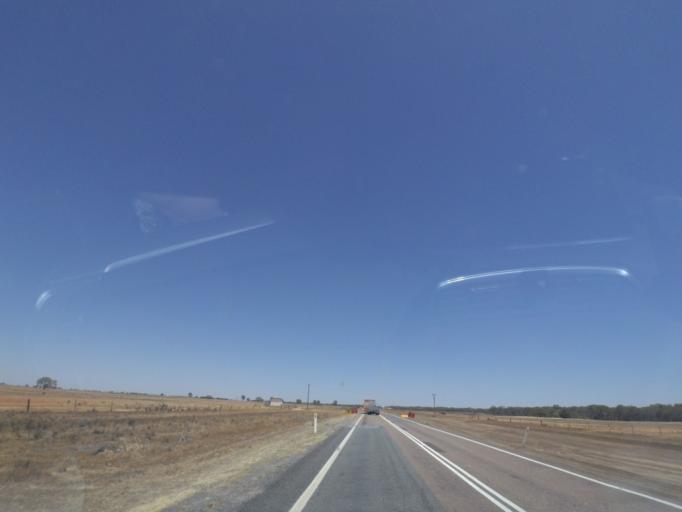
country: AU
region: New South Wales
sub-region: Berrigan
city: Berrigan
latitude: -35.1495
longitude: 145.9932
